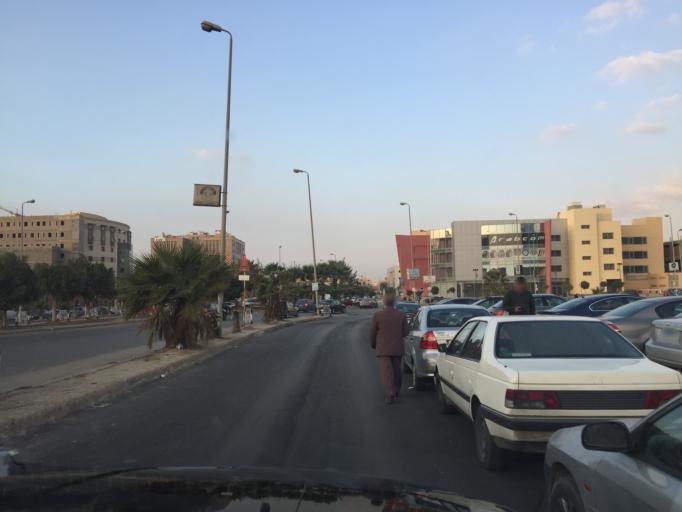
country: EG
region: Muhafazat al Qahirah
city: Cairo
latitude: 30.0175
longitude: 31.4178
